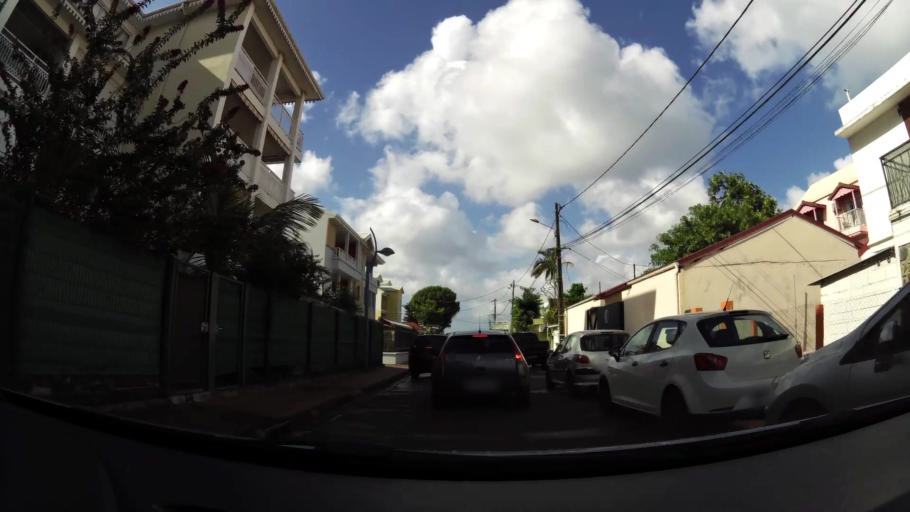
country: MQ
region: Martinique
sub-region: Martinique
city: Les Trois-Ilets
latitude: 14.5502
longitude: -61.0540
